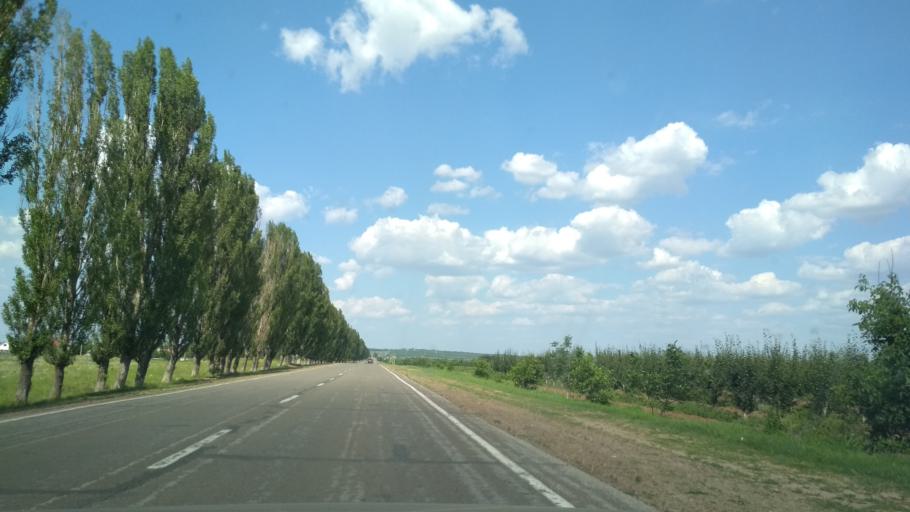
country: MD
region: Chisinau
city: Vadul lui Voda
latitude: 47.1279
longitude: 29.1219
